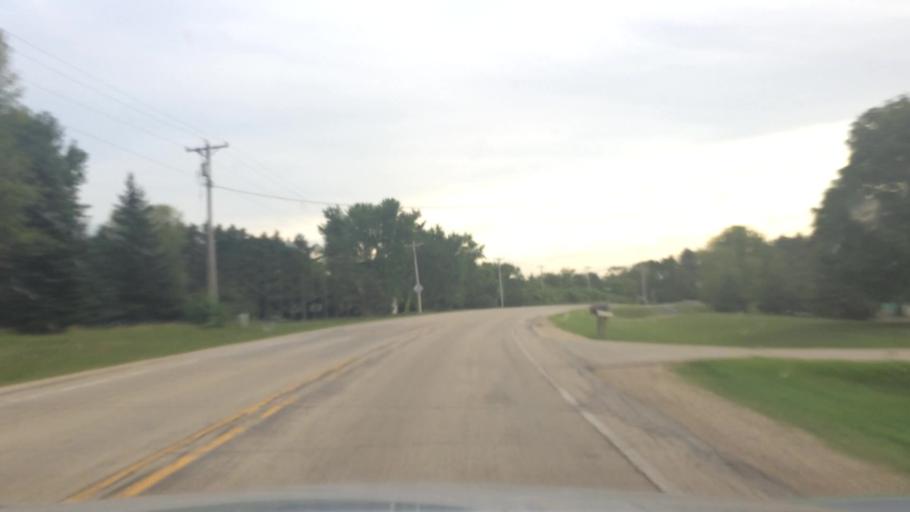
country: US
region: Wisconsin
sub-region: Dane County
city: Waunakee
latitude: 43.2003
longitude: -89.5519
